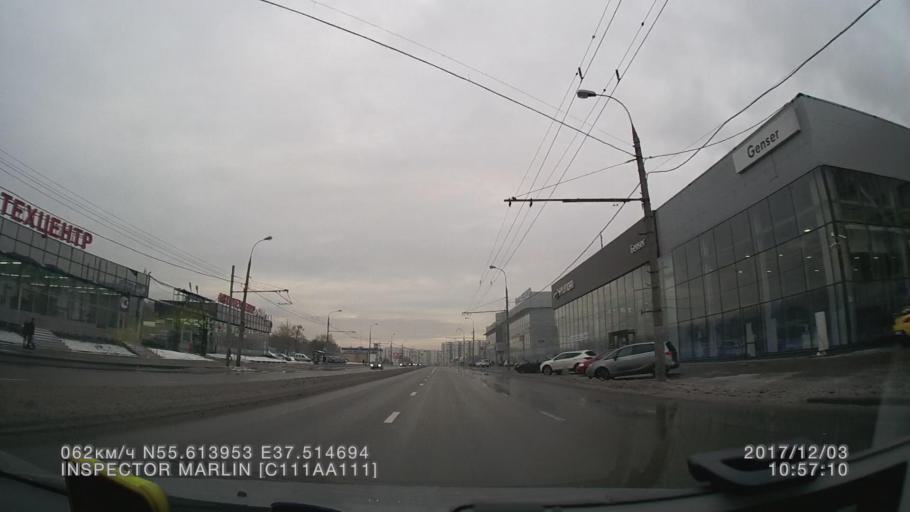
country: RU
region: Moscow
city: Yasenevo
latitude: 55.6138
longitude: 37.5150
